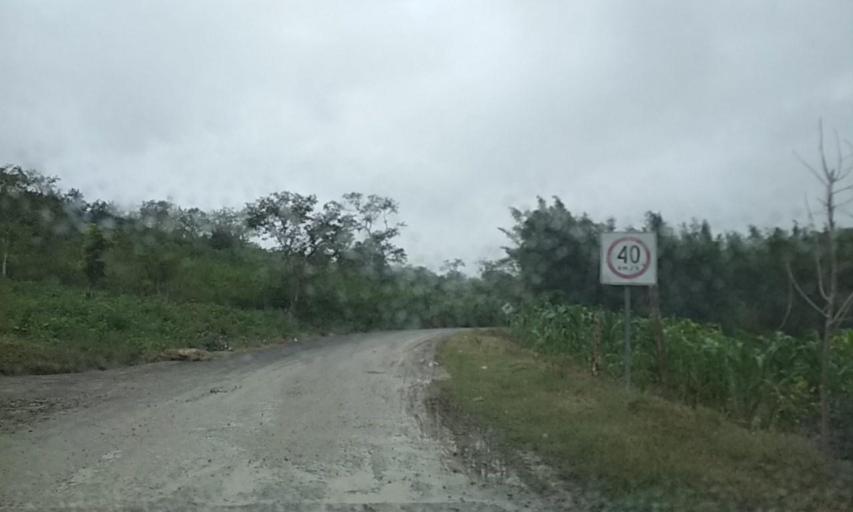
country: MX
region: Veracruz
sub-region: Papantla
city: El Chote
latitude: 20.3943
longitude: -97.3573
